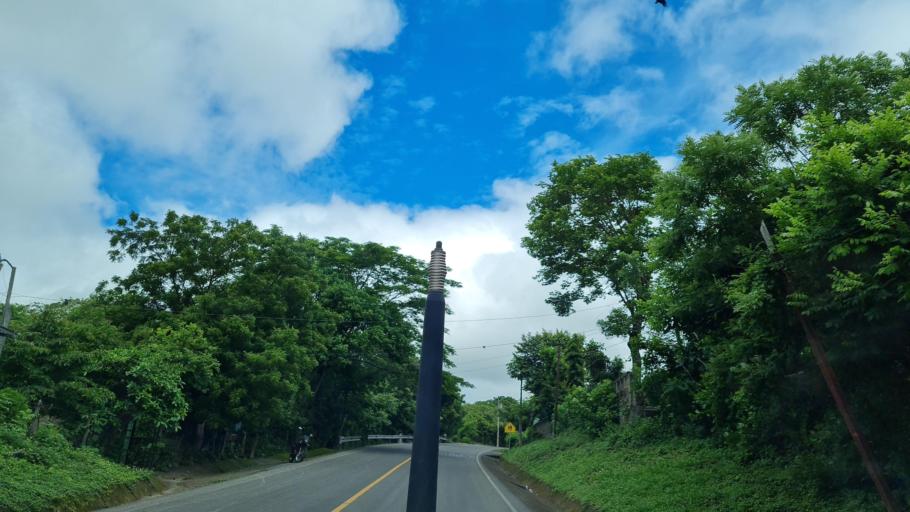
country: NI
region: Boaco
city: San Jose de los Remates
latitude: 12.5905
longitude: -85.9057
